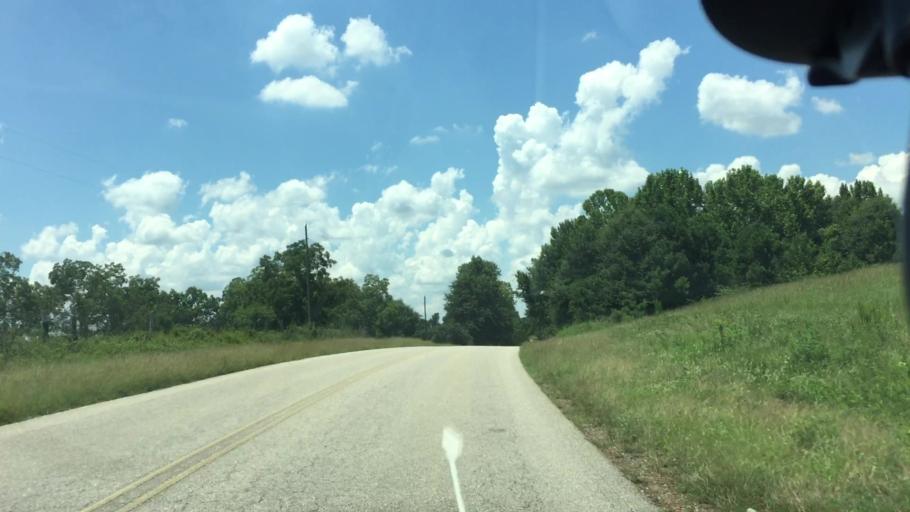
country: US
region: Alabama
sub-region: Pike County
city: Troy
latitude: 31.7457
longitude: -85.9631
